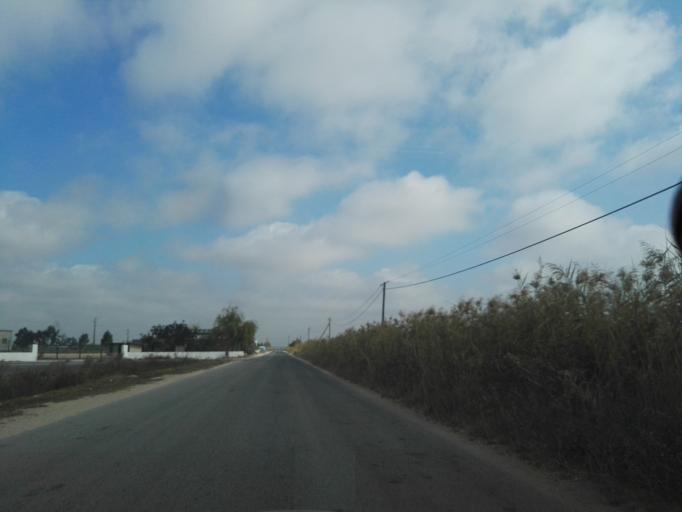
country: PT
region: Santarem
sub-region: Benavente
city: Samora Correia
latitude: 38.9657
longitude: -8.9089
